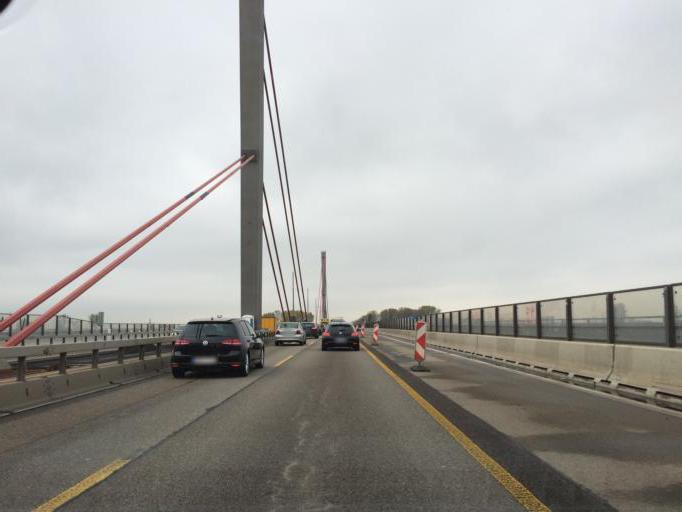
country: DE
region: North Rhine-Westphalia
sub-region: Regierungsbezirk Koln
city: Leverkusen
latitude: 51.0355
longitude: 6.9631
